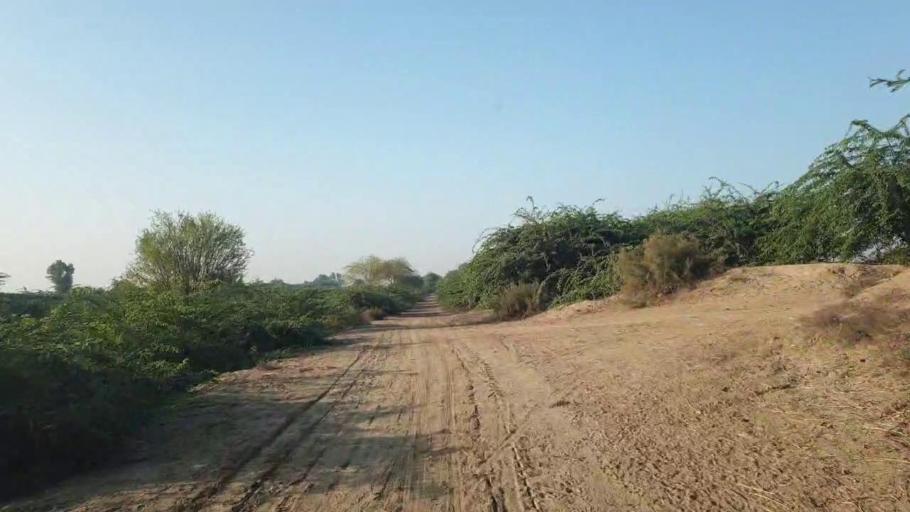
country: PK
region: Sindh
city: Badin
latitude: 24.6060
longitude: 68.7807
